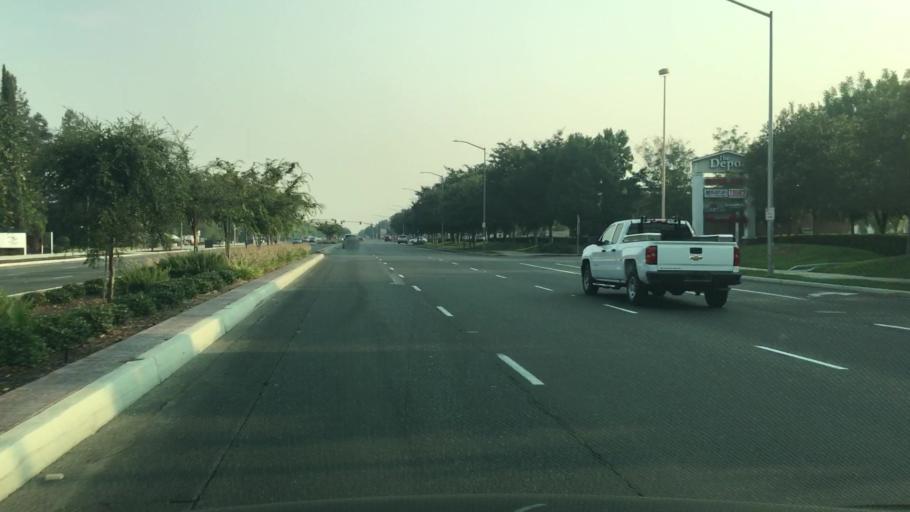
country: US
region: California
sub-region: Fresno County
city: Clovis
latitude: 36.8494
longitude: -119.7297
